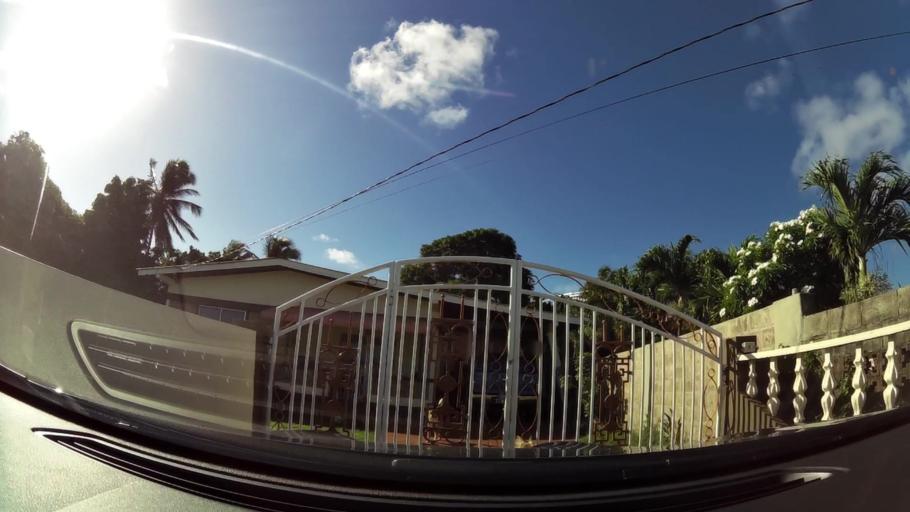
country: TT
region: Tobago
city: Scarborough
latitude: 11.1489
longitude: -60.8341
